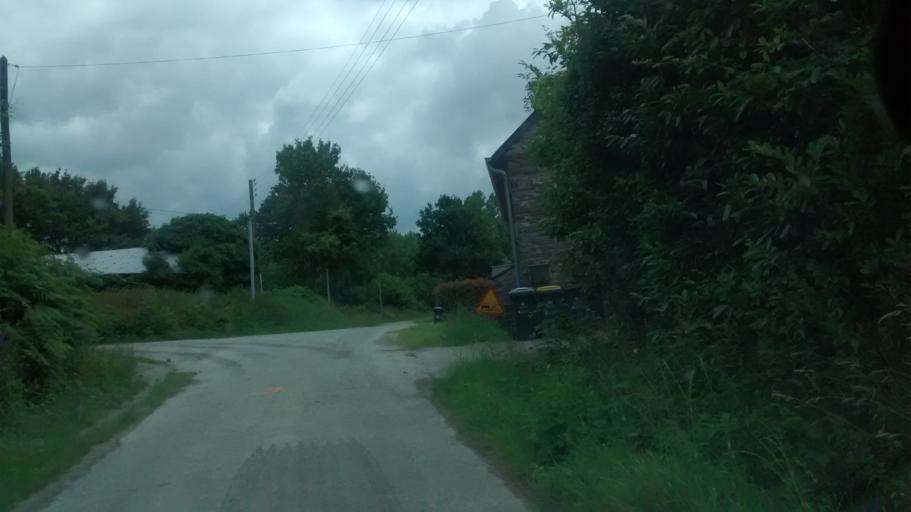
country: FR
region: Brittany
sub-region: Departement d'Ille-et-Vilaine
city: La Dominelais
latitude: 47.7763
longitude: -1.7379
